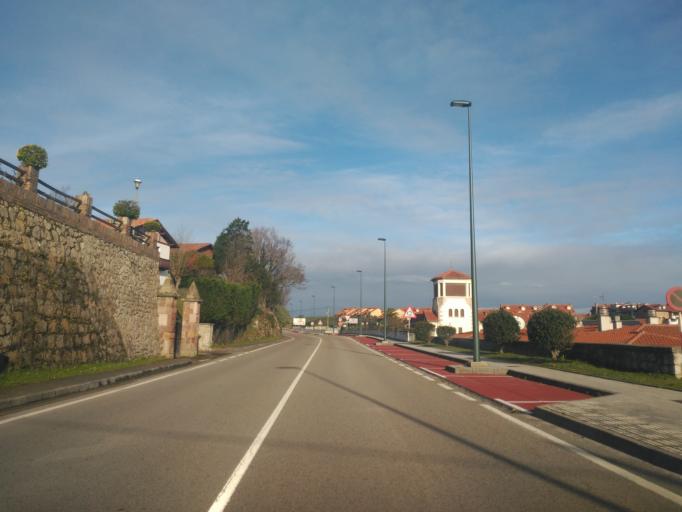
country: ES
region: Cantabria
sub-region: Provincia de Cantabria
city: Comillas
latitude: 43.3893
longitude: -4.2903
